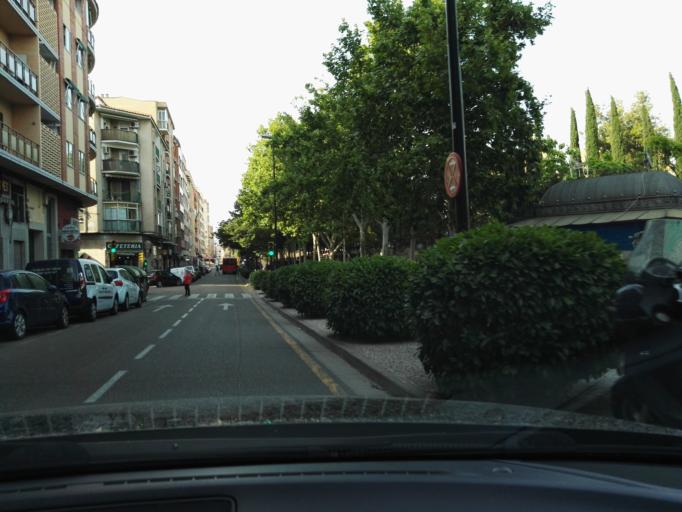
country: ES
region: Aragon
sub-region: Provincia de Zaragoza
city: Zaragoza
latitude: 41.6378
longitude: -0.8743
